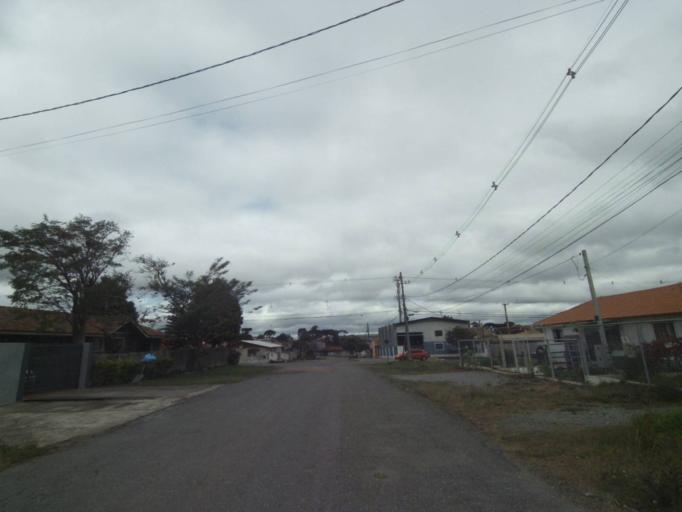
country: BR
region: Parana
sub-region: Sao Jose Dos Pinhais
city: Sao Jose dos Pinhais
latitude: -25.5348
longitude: -49.2991
